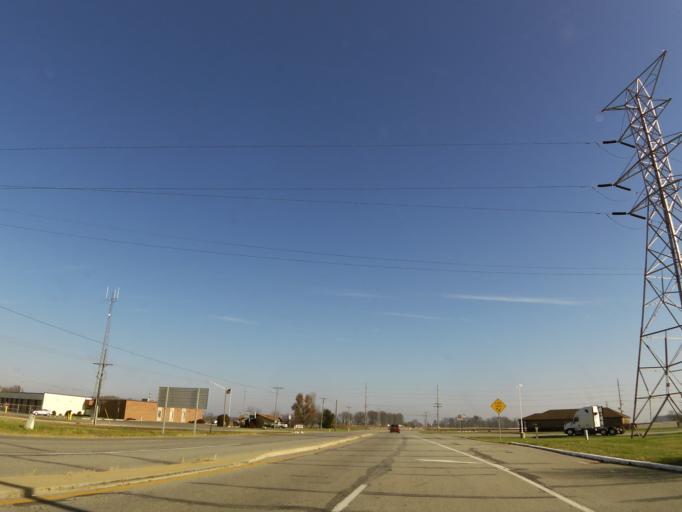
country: US
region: Indiana
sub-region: Shelby County
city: Shelbyville
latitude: 39.5273
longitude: -85.7337
